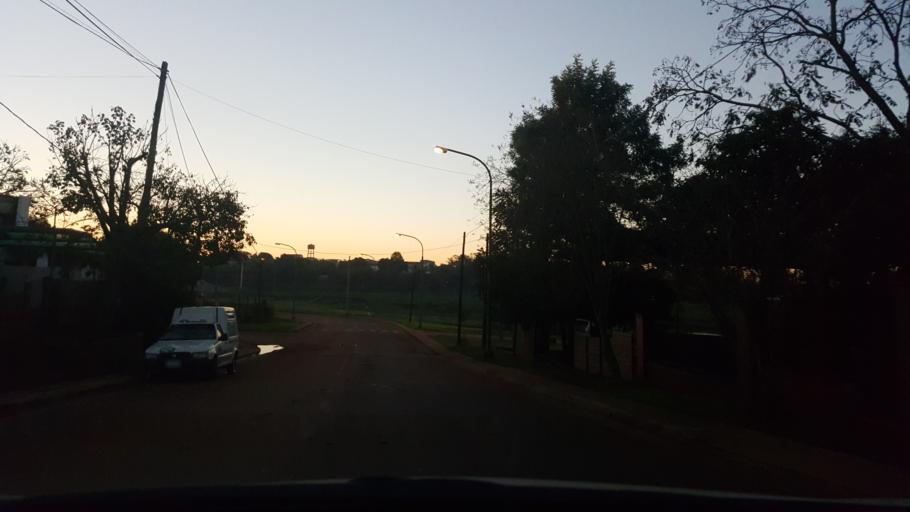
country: AR
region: Misiones
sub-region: Departamento de Capital
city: Posadas
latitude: -27.4218
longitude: -55.9009
